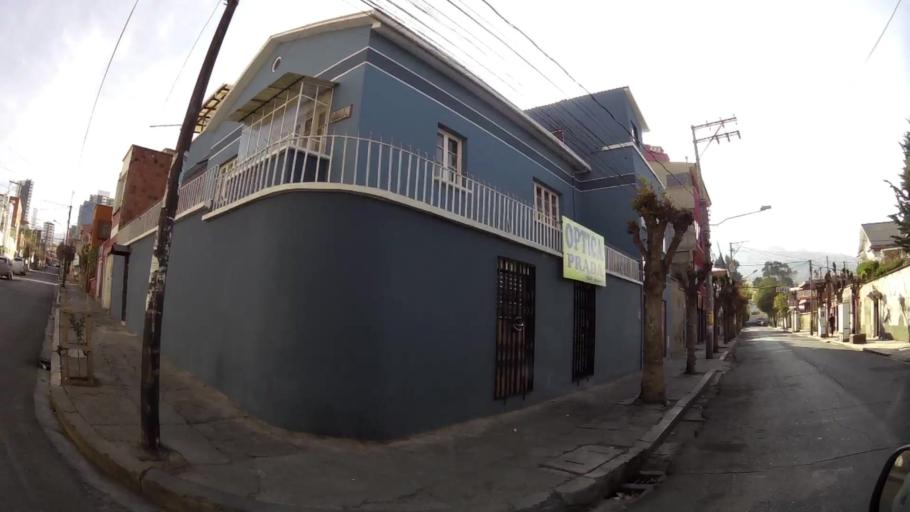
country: BO
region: La Paz
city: La Paz
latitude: -16.5058
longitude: -68.1189
